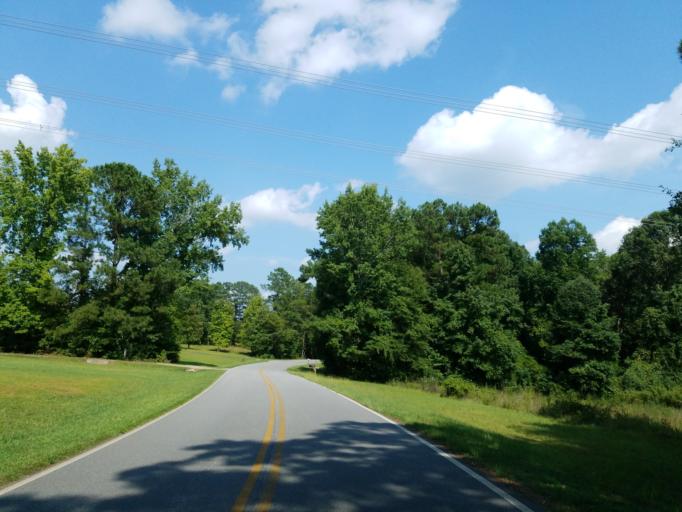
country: US
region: Georgia
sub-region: Monroe County
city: Forsyth
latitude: 33.0111
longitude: -83.8567
